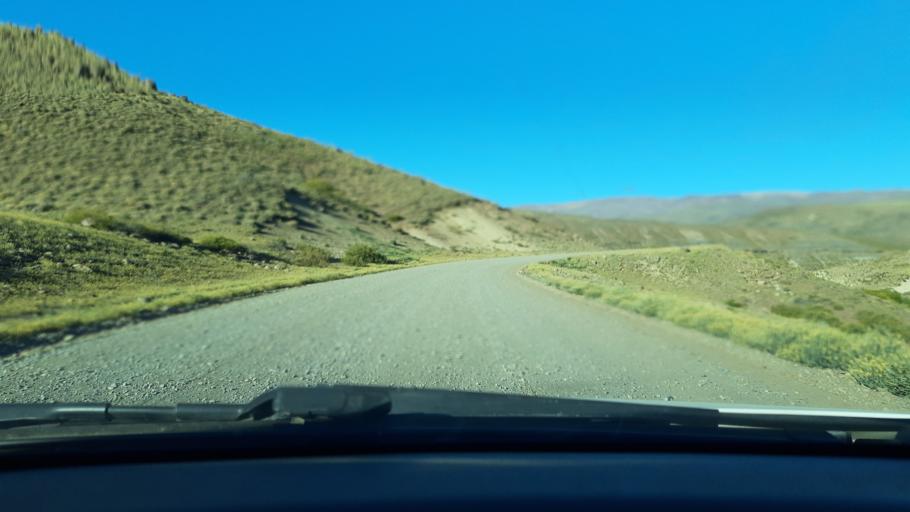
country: AR
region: Neuquen
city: Las Ovejas
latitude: -36.8216
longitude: -70.7042
